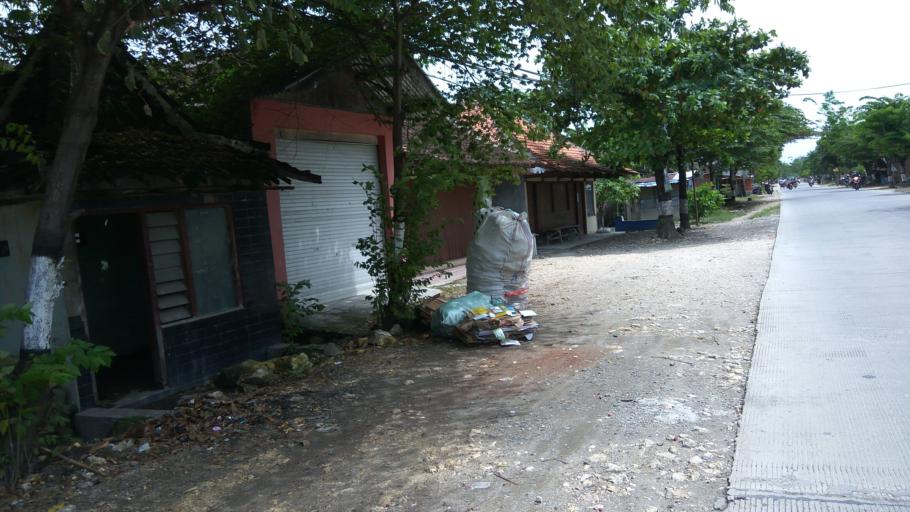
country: ID
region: Central Java
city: Mranggen
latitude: -7.0655
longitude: 110.6656
